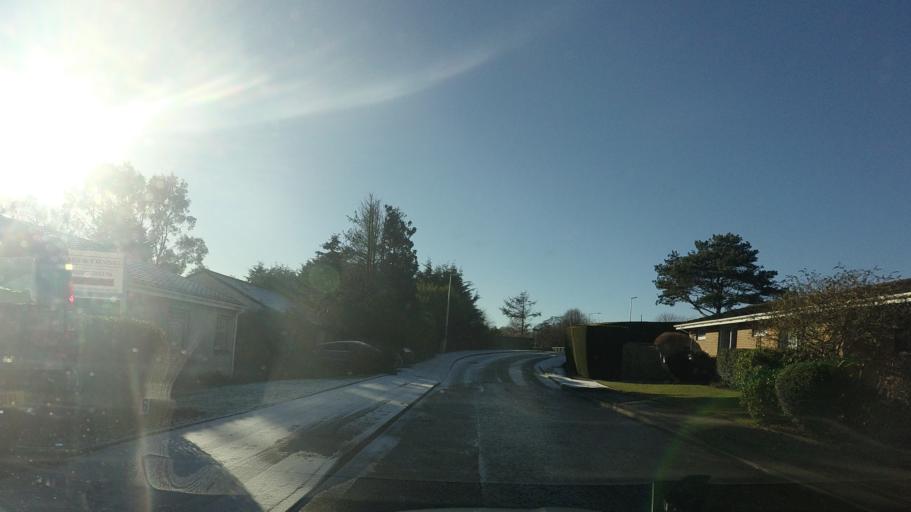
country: GB
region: Scotland
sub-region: Fife
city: Crossgates
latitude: 56.0379
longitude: -3.3471
